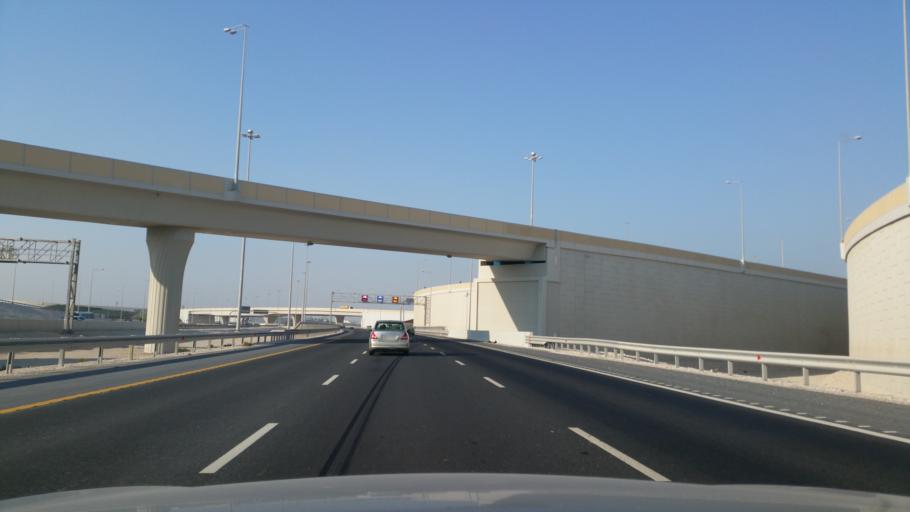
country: QA
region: Al Wakrah
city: Al Wakrah
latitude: 25.1223
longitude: 51.5878
